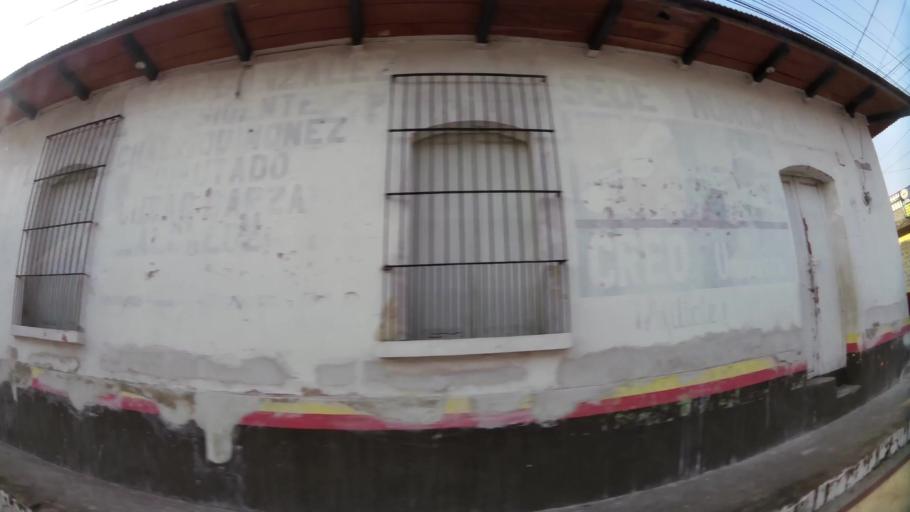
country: GT
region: Retalhuleu
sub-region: Municipio de Retalhuleu
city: Retalhuleu
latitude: 14.5389
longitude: -91.6771
